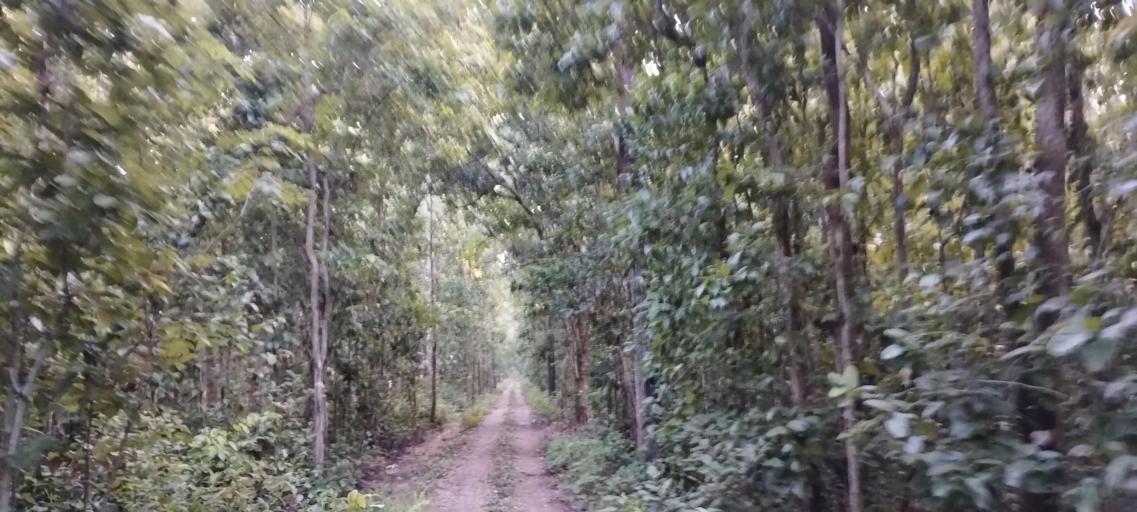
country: NP
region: Far Western
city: Tikapur
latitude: 28.4834
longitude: 81.2619
